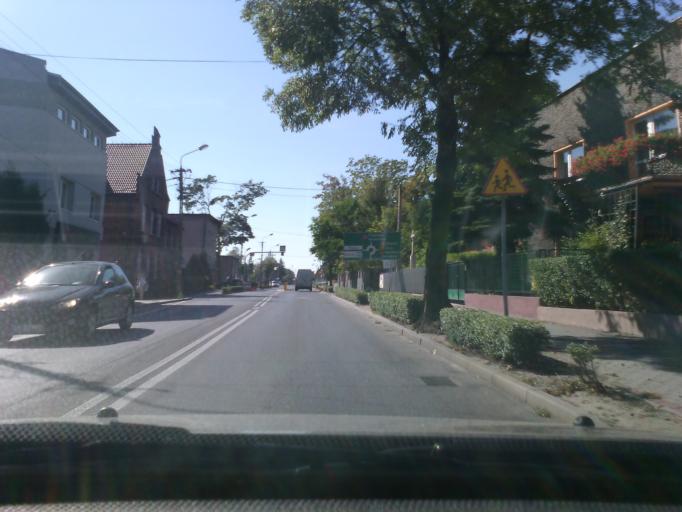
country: PL
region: Silesian Voivodeship
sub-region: Rybnik
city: Rybnik
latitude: 50.0913
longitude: 18.5338
